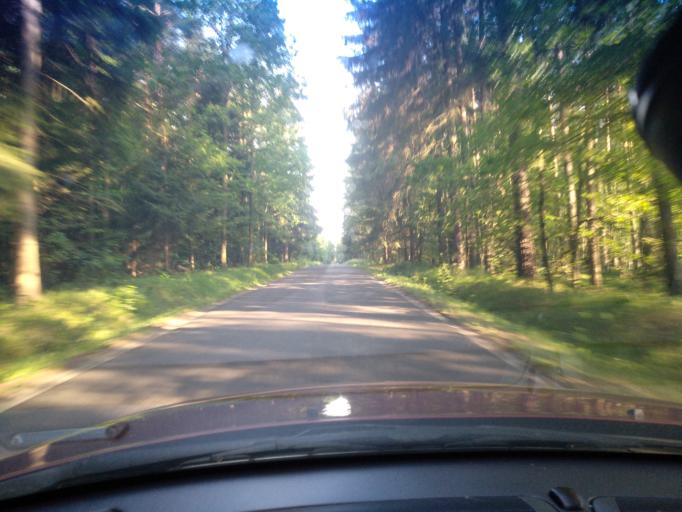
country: PL
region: Lower Silesian Voivodeship
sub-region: Powiat lubanski
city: Swieradow-Zdroj
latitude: 50.9608
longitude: 15.3017
